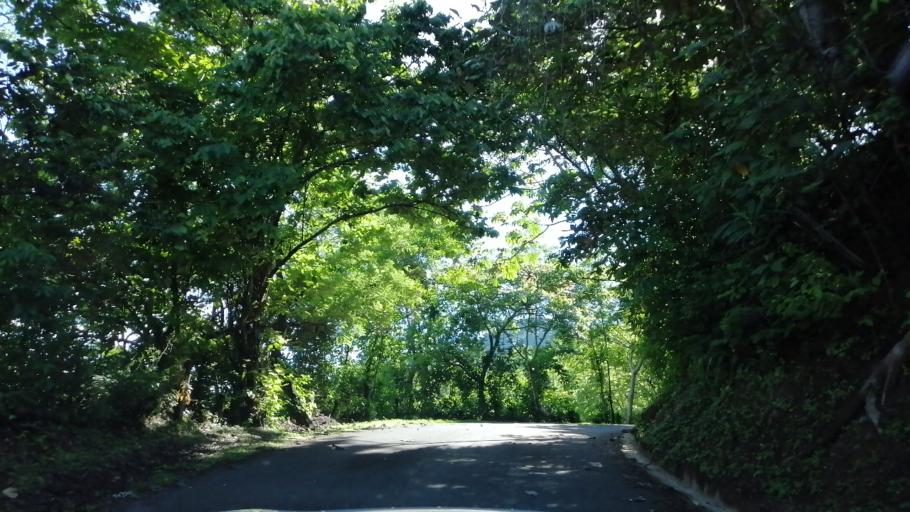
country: SV
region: Morazan
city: Cacaopera
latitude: 13.7871
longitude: -88.0296
